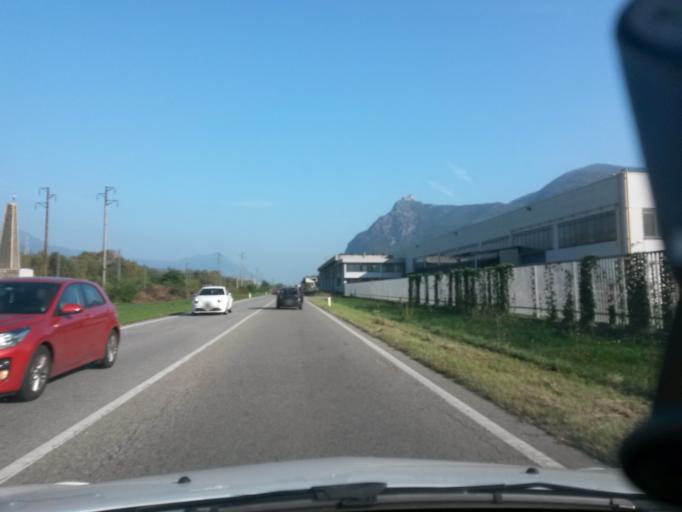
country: IT
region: Piedmont
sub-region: Provincia di Torino
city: Vaie
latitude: 45.1070
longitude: 7.2998
